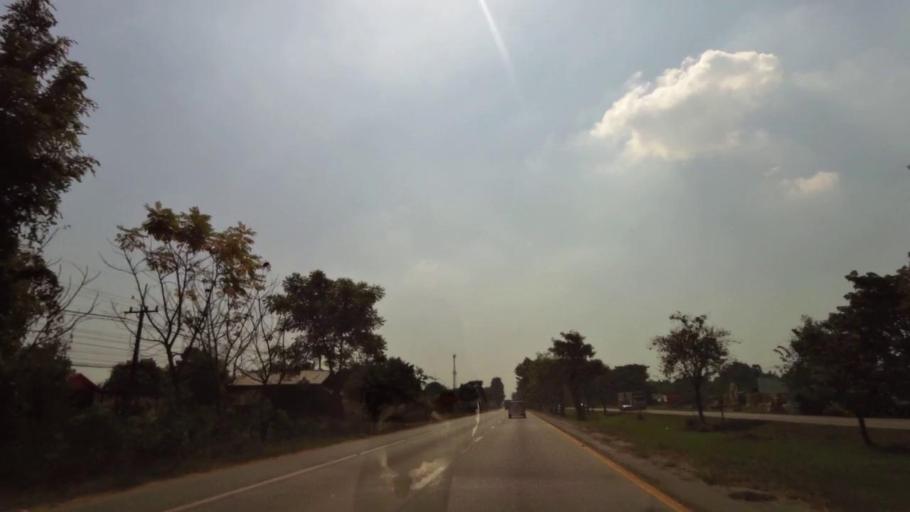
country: TH
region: Phichit
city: Wachira Barami
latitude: 16.5358
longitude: 100.1442
